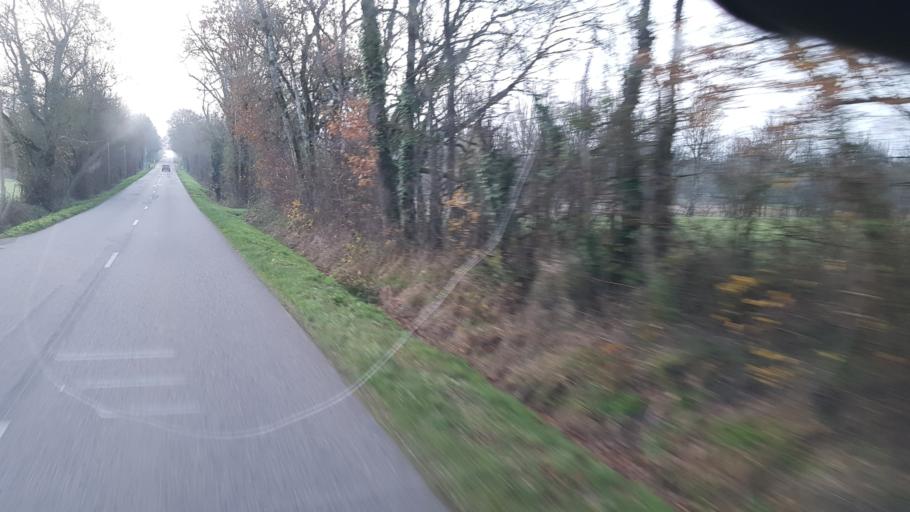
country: FR
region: Midi-Pyrenees
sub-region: Departement du Tarn-et-Garonne
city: Montricoux
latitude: 44.1041
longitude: 1.5988
